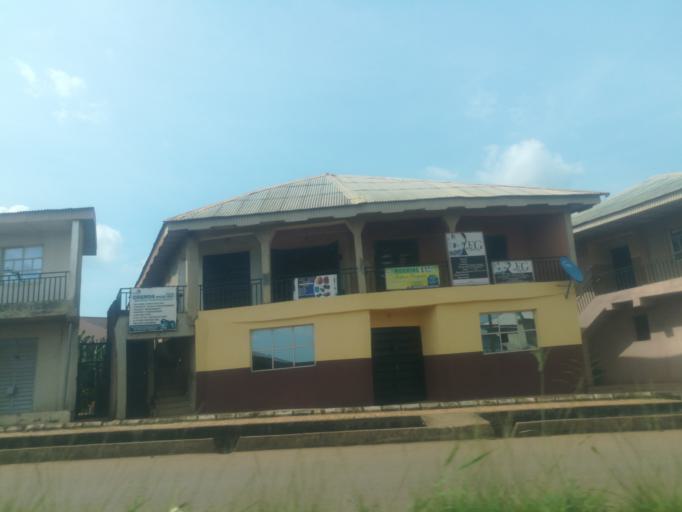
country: NG
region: Ogun
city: Abeokuta
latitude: 7.1675
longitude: 3.3802
